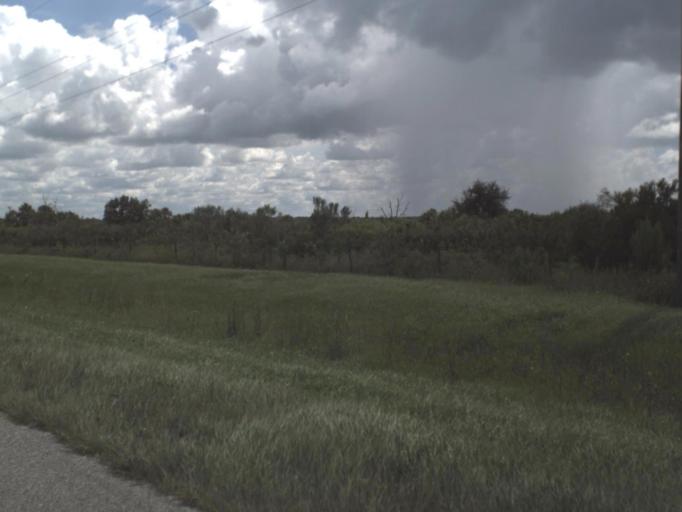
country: US
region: Florida
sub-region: Polk County
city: Babson Park
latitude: 27.8440
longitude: -81.3588
